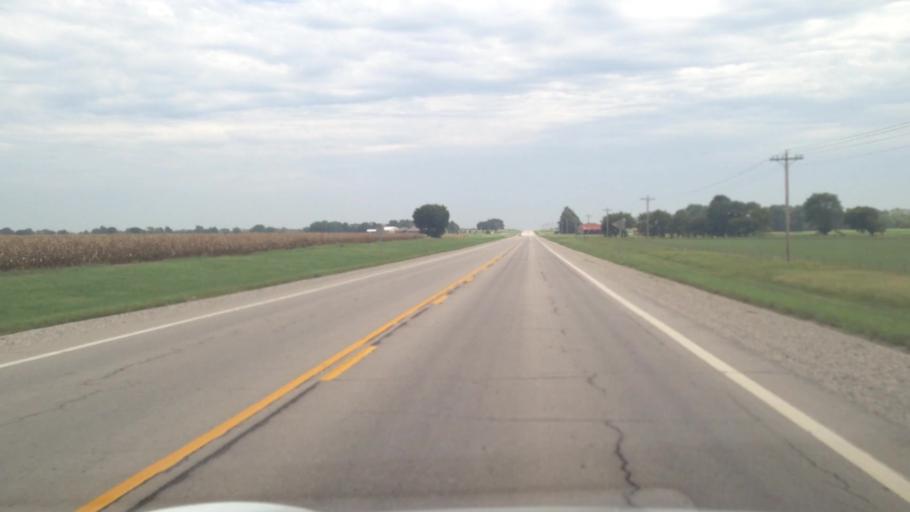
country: US
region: Kansas
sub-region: Crawford County
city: Girard
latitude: 37.5144
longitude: -94.9419
